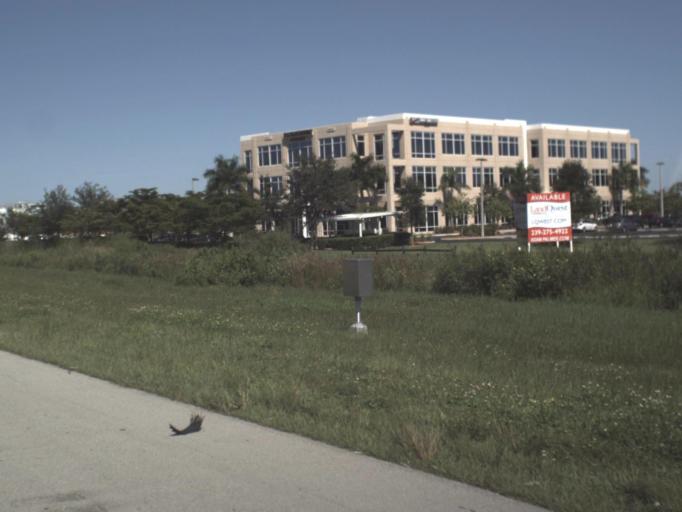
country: US
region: Florida
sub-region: Lee County
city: Fort Myers
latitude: 26.6260
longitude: -81.8053
